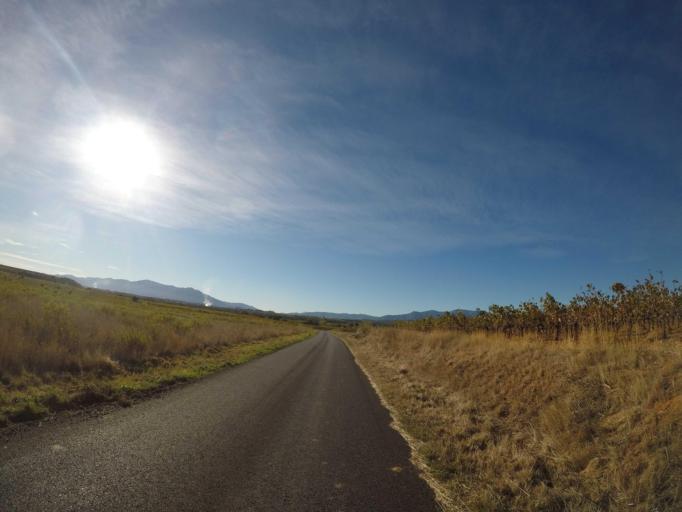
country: FR
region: Languedoc-Roussillon
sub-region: Departement des Pyrenees-Orientales
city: Llupia
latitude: 42.5930
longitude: 2.7643
